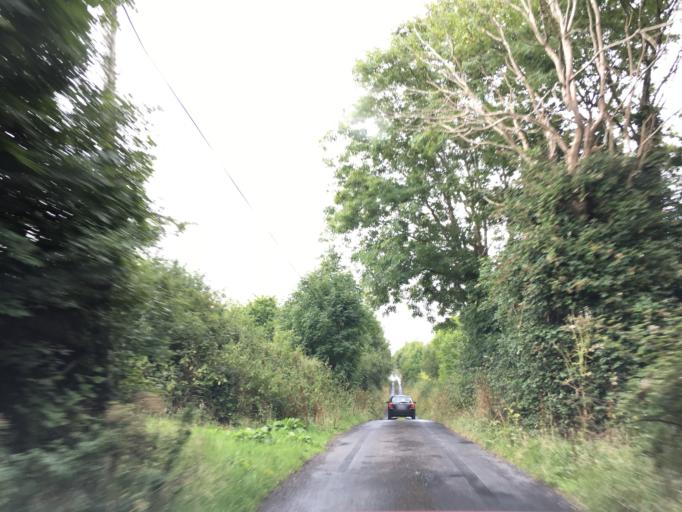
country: IE
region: Munster
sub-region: An Clar
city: Ennis
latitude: 52.7291
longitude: -9.0867
